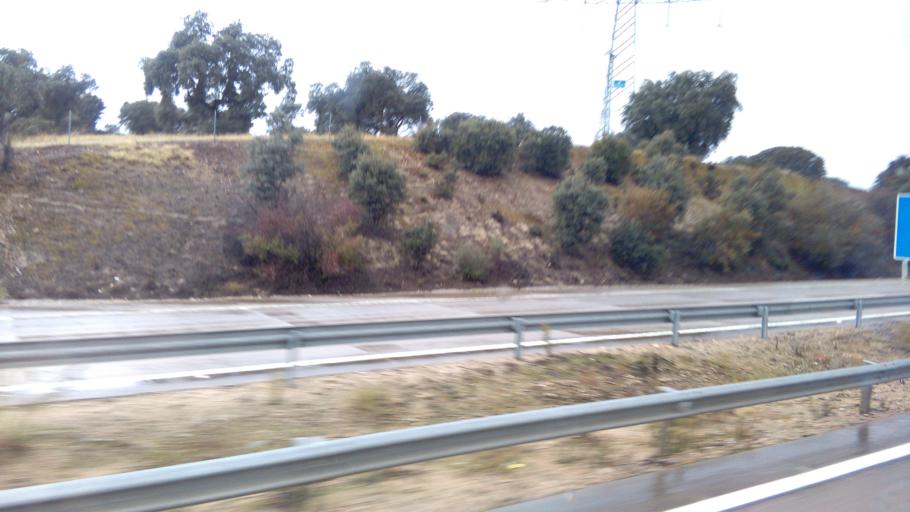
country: ES
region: Castille-La Mancha
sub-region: Province of Toledo
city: Cervera de los Montes
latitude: 40.0085
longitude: -4.7738
